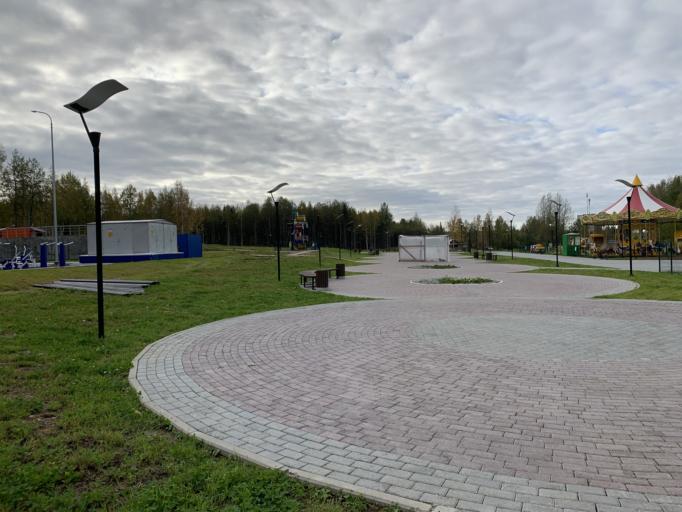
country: RU
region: Perm
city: Gubakha
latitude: 58.8337
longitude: 57.5609
